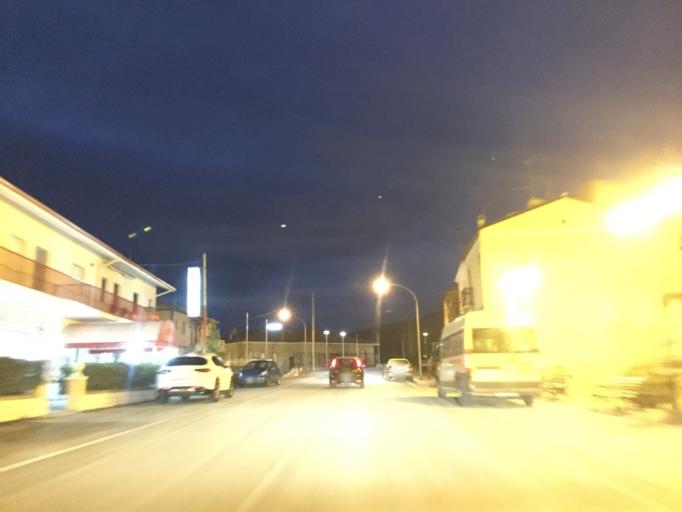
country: IT
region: Apulia
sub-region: Provincia di Foggia
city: Volturara Appula
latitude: 41.4968
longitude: 15.0545
